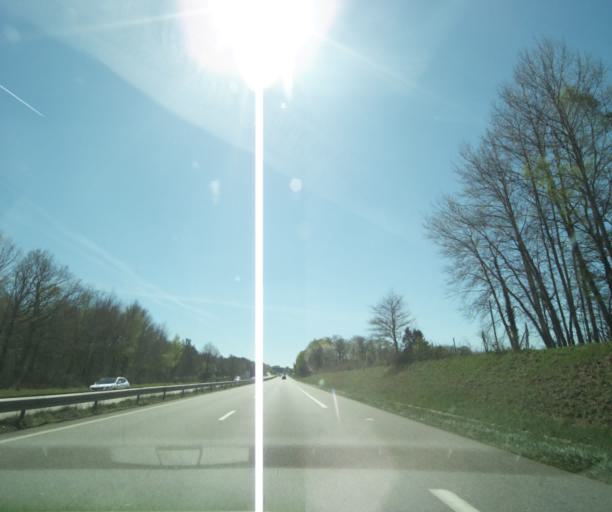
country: FR
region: Limousin
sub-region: Departement de la Haute-Vienne
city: Rilhac-Rancon
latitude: 45.9020
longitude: 1.2919
